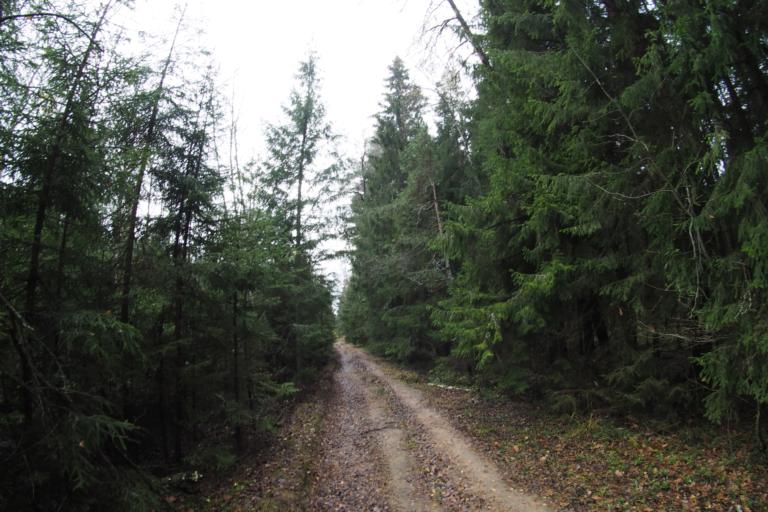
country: RU
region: Moskovskaya
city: Davydovo
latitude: 55.5639
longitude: 38.7649
